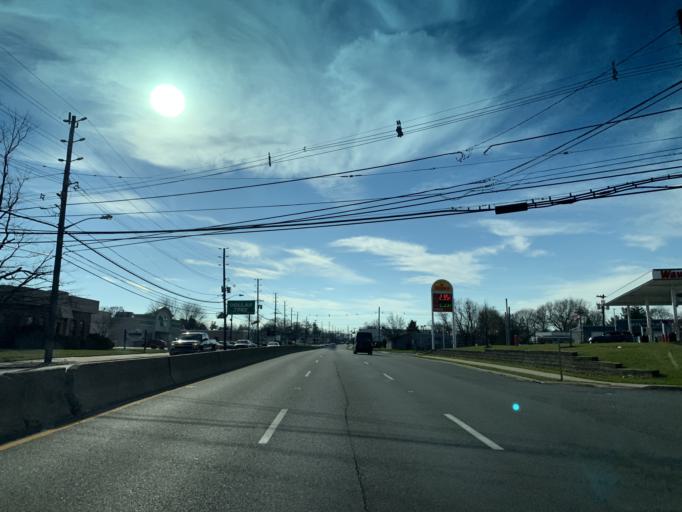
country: US
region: New Jersey
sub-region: Camden County
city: Pennsauken
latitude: 39.9642
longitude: -75.0495
